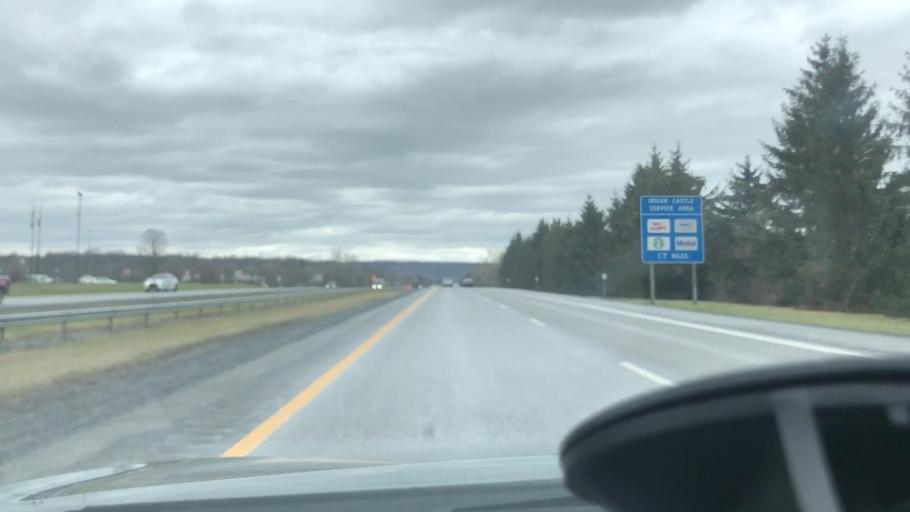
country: US
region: New York
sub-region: Herkimer County
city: Frankfort
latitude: 43.0764
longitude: -75.1048
